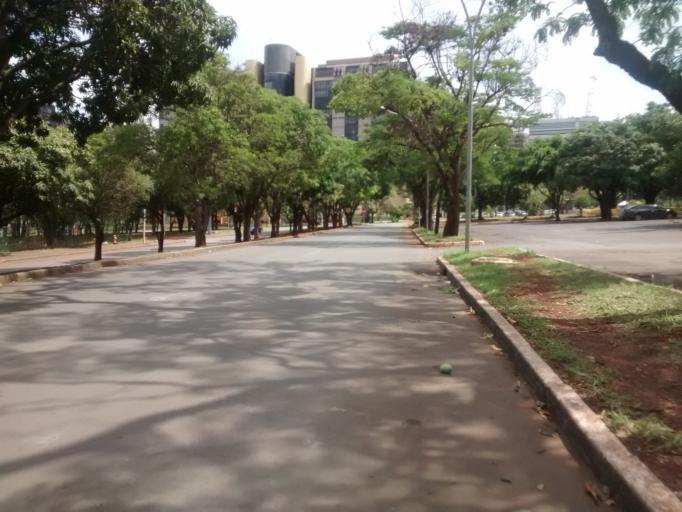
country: BR
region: Federal District
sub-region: Brasilia
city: Brasilia
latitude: -15.7848
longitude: -47.8844
